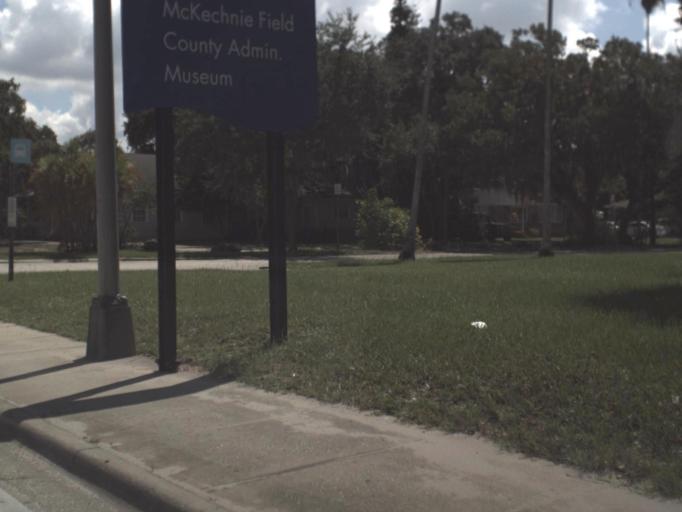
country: US
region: Florida
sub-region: Manatee County
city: West Bradenton
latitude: 27.4956
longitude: -82.5956
